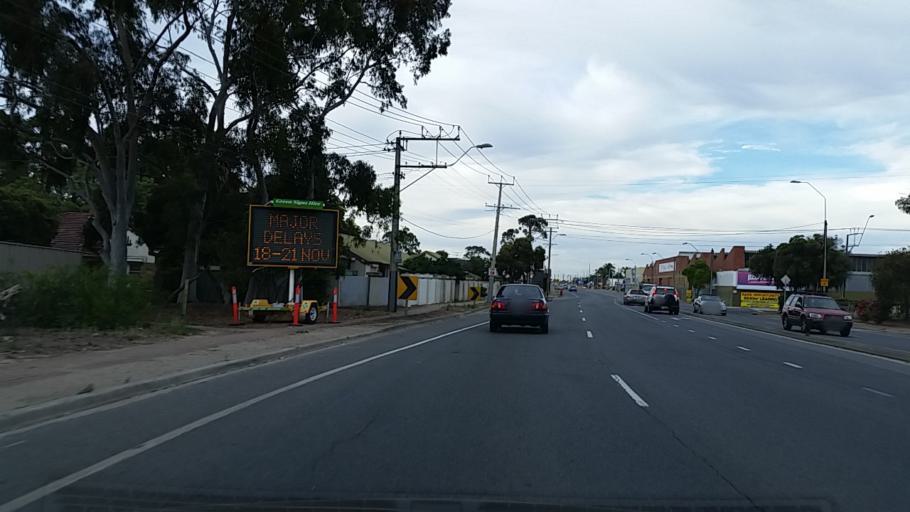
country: AU
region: South Australia
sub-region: City of West Torrens
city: Thebarton
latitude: -34.9116
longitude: 138.5644
